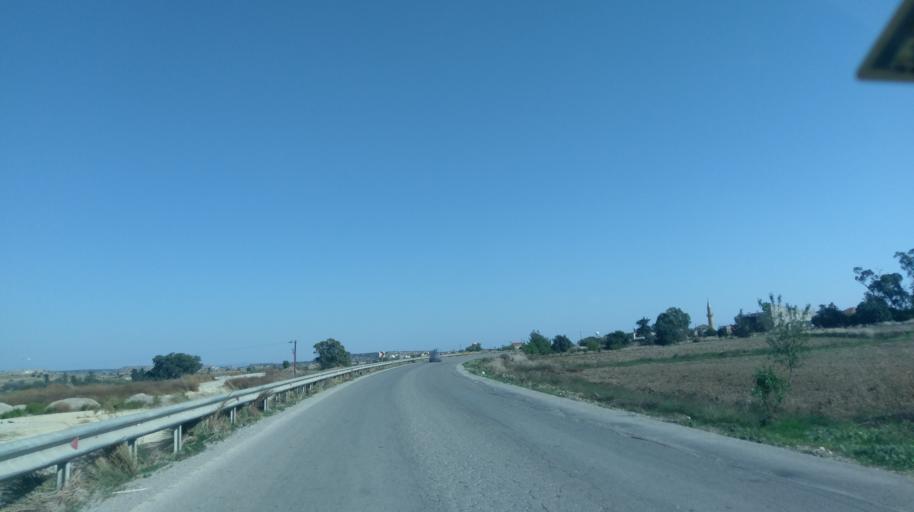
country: CY
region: Ammochostos
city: Leonarisso
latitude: 35.3680
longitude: 34.0250
